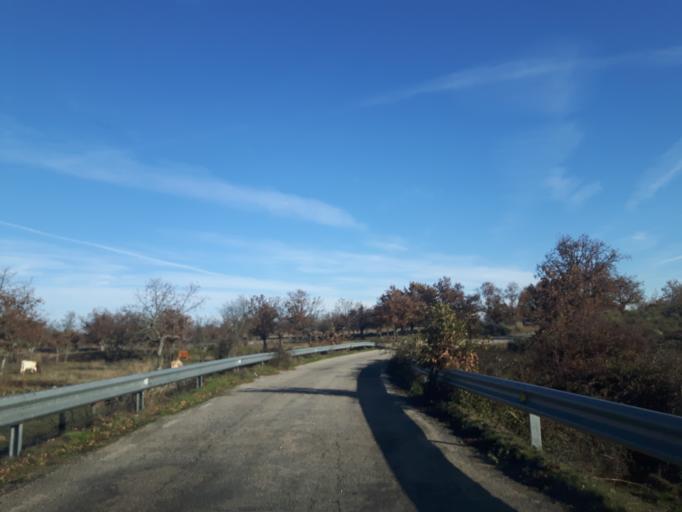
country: ES
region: Castille and Leon
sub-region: Provincia de Salamanca
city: Cerralbo
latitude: 40.9548
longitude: -6.6024
